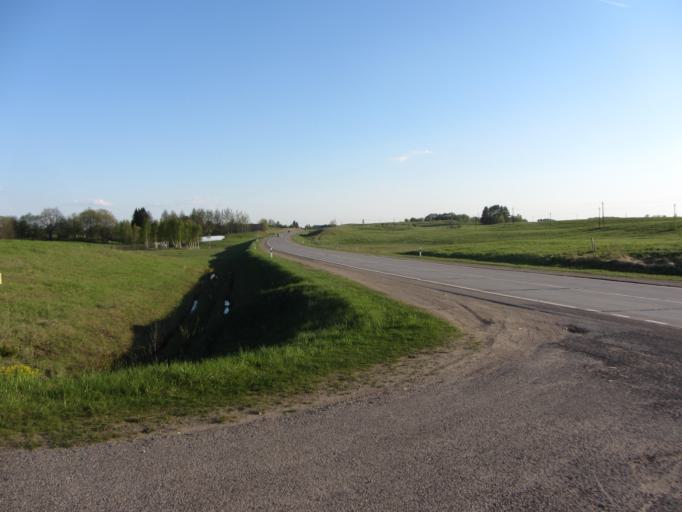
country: LT
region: Utenos apskritis
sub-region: Utena
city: Utena
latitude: 55.3799
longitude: 25.5201
